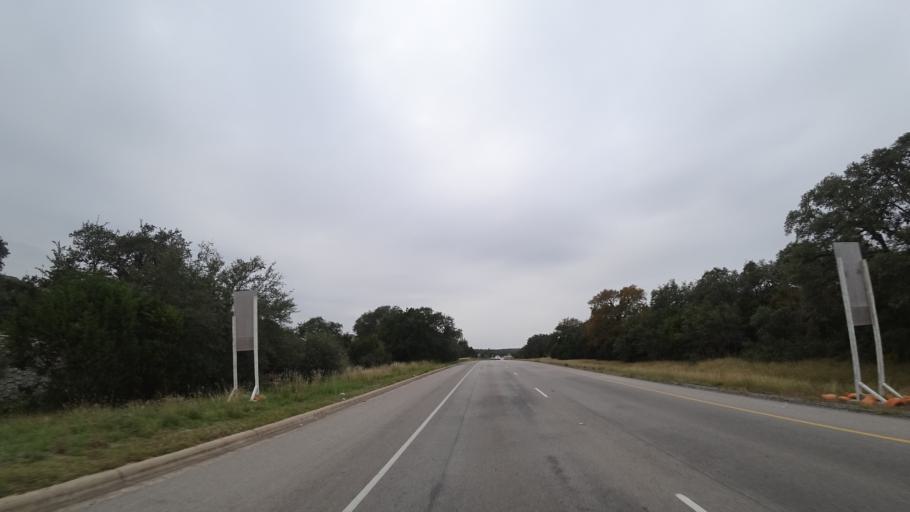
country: US
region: Texas
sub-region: Travis County
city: Shady Hollow
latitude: 30.1837
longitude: -97.9069
